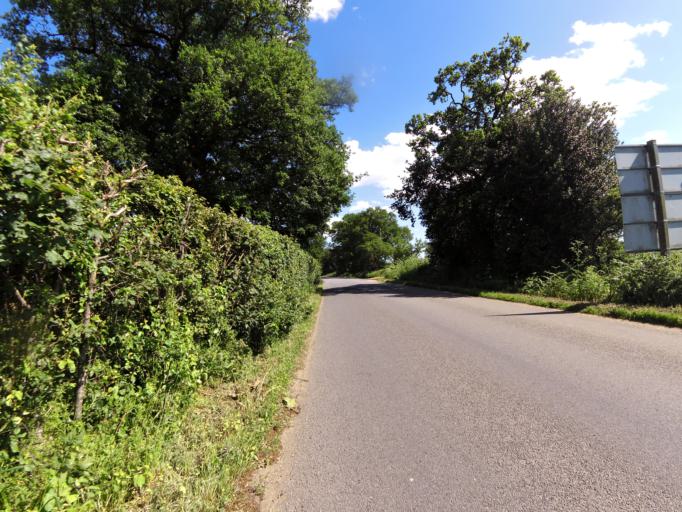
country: GB
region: England
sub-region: Suffolk
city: Kesgrave
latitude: 52.0244
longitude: 1.2090
